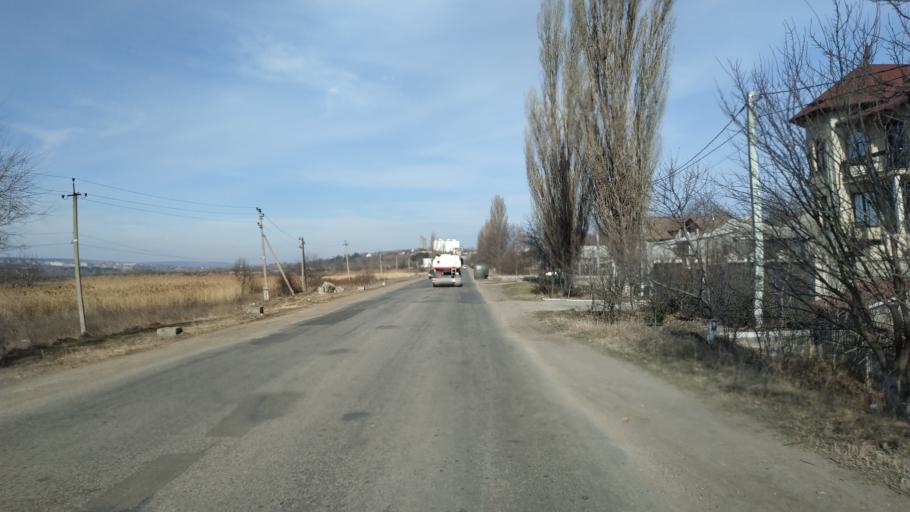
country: MD
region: Laloveni
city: Ialoveni
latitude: 46.9457
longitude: 28.7724
